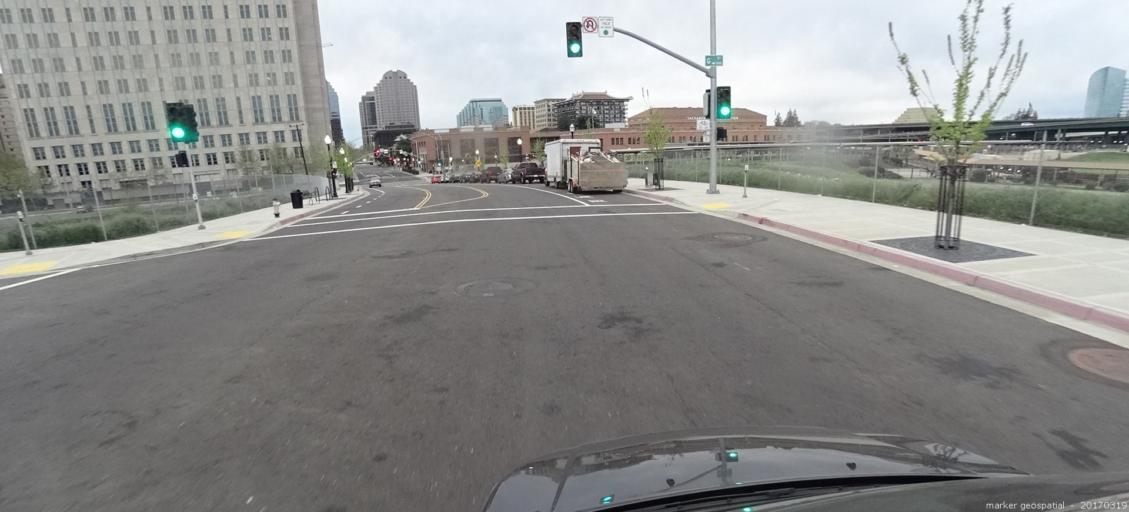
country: US
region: California
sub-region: Sacramento County
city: Sacramento
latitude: 38.5854
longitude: -121.4985
